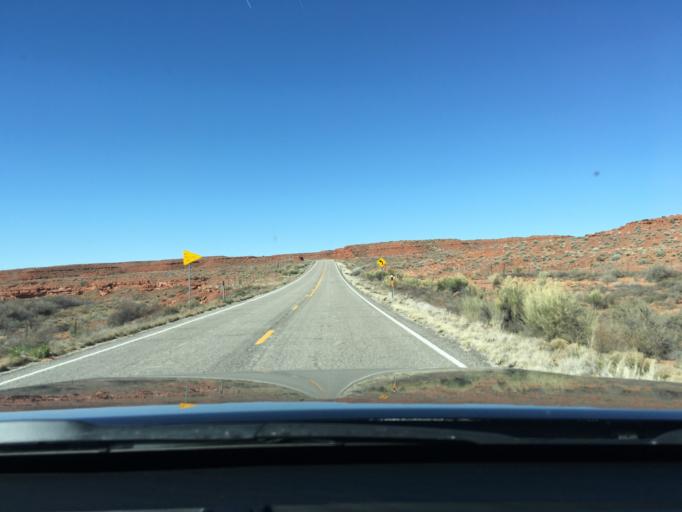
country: US
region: Utah
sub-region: San Juan County
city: Blanding
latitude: 37.2143
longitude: -109.8417
